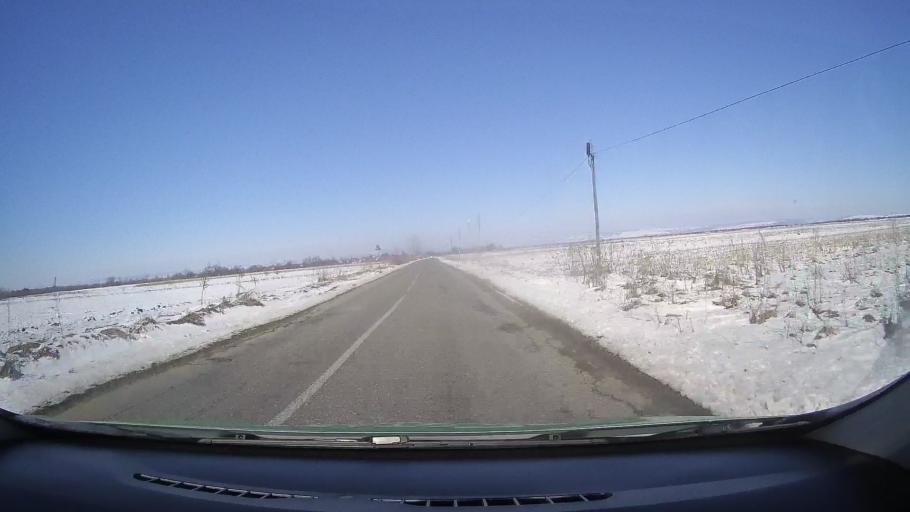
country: RO
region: Brasov
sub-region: Comuna Harseni
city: Harseni
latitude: 45.7442
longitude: 25.0183
